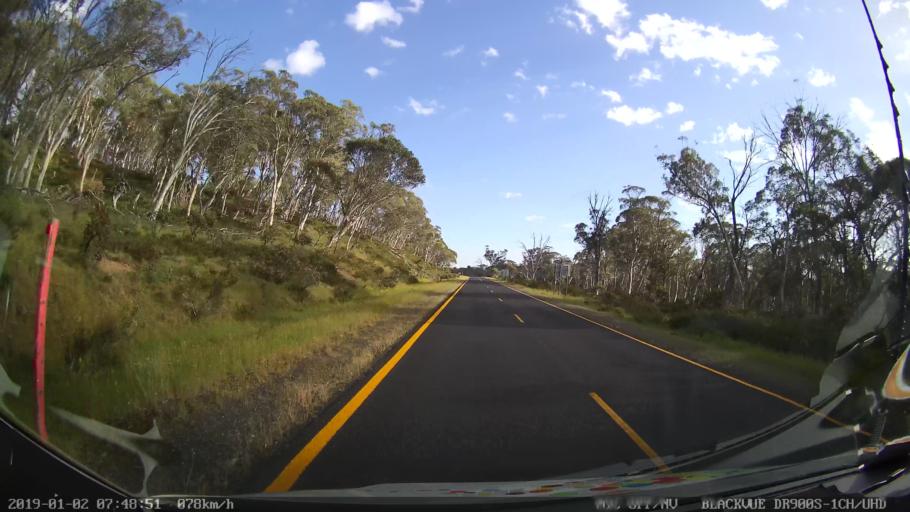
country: AU
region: New South Wales
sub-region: Tumut Shire
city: Tumut
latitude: -35.7484
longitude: 148.5201
